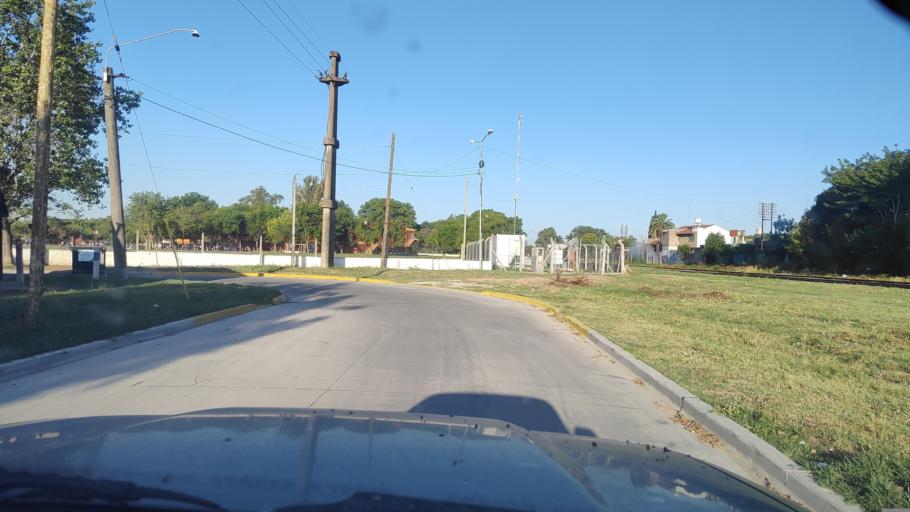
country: AR
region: Buenos Aires
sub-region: Partido de Lujan
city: Lujan
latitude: -34.5793
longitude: -59.1100
